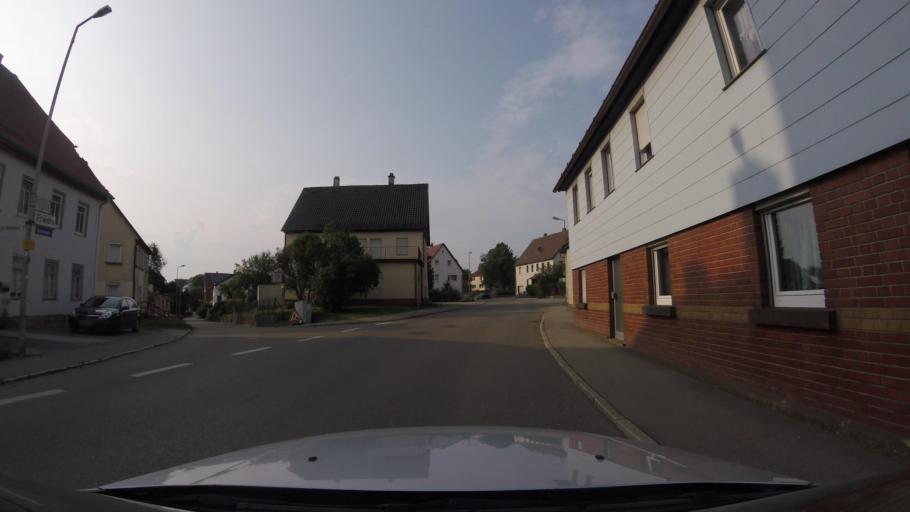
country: DE
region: Baden-Wuerttemberg
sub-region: Regierungsbezirk Stuttgart
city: Alfdorf
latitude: 48.8399
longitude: 9.6822
